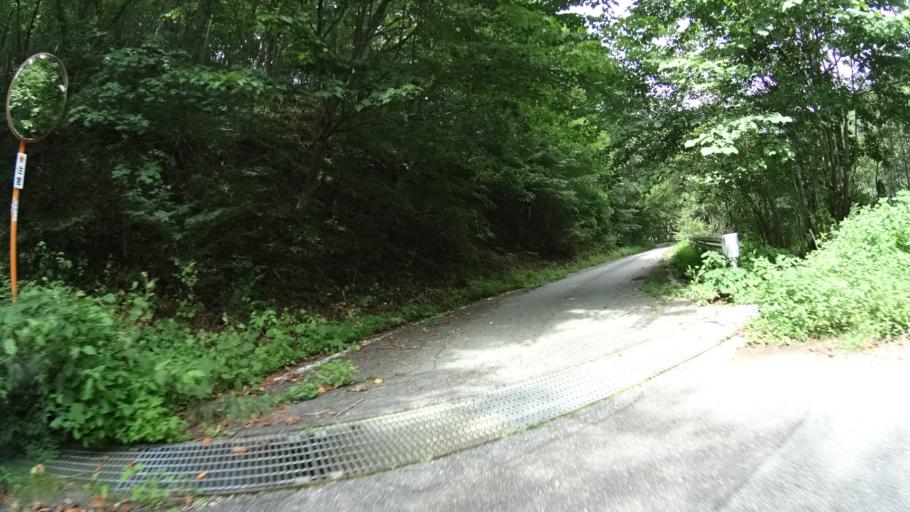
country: JP
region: Yamanashi
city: Nirasaki
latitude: 35.8043
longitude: 138.5431
